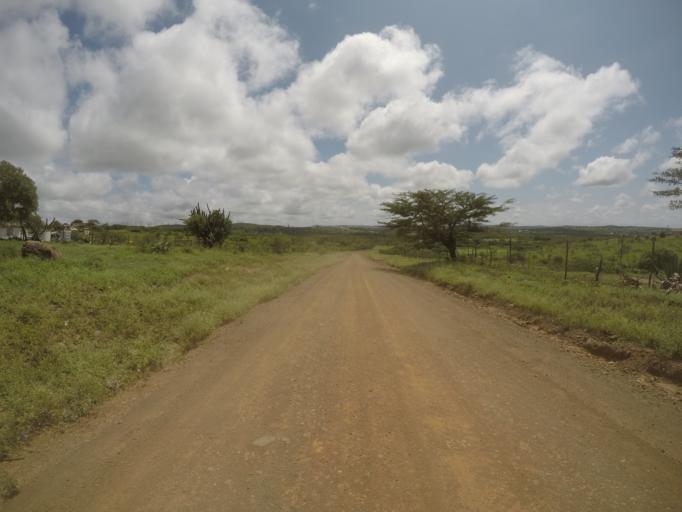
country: ZA
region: KwaZulu-Natal
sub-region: uThungulu District Municipality
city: Empangeni
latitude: -28.5752
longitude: 31.8376
